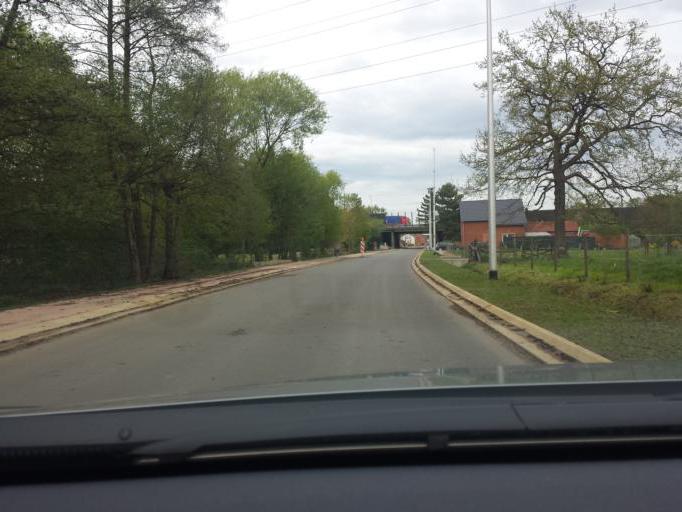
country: BE
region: Flanders
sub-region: Provincie Limburg
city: Lummen
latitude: 51.0033
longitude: 5.2176
